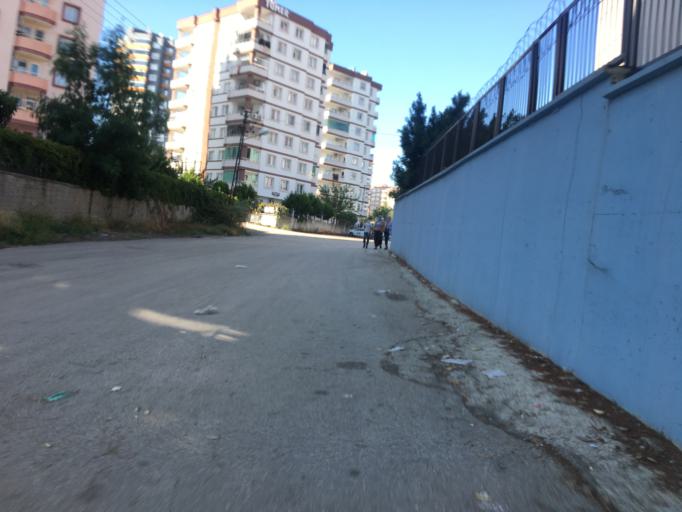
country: TR
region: Adana
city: Seyhan
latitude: 37.0299
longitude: 35.2860
